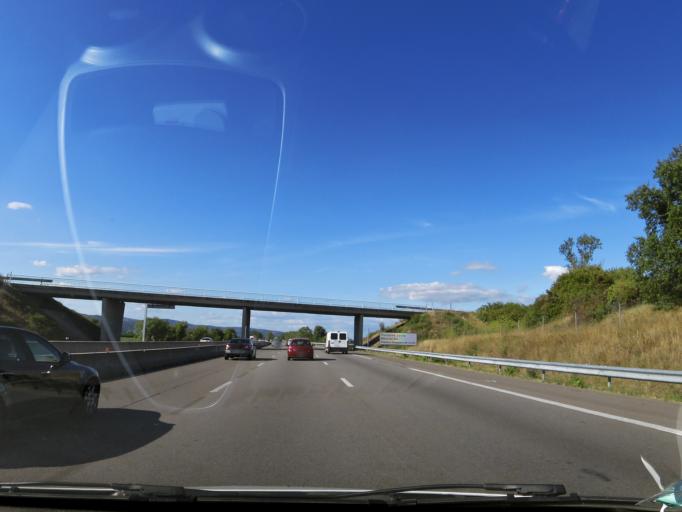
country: FR
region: Rhone-Alpes
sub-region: Departement de la Drome
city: Saulce-sur-Rhone
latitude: 44.7333
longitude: 4.7895
